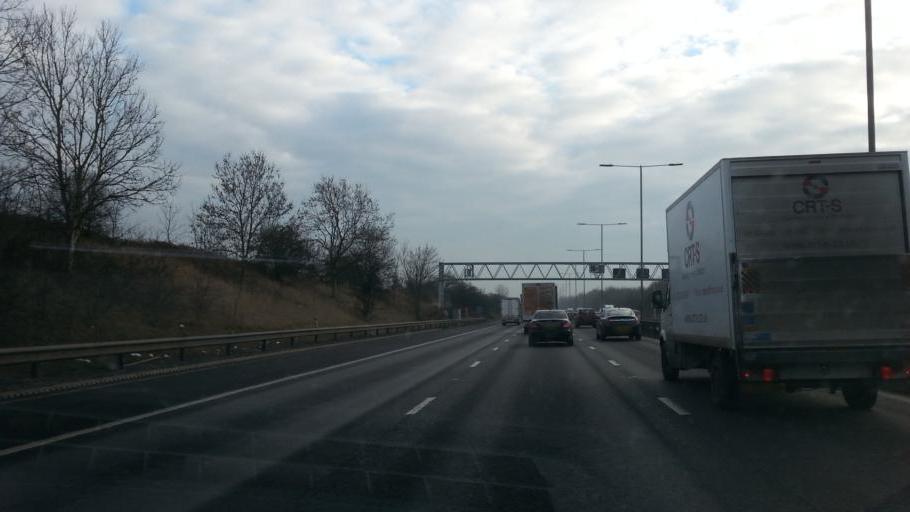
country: GB
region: England
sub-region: Warwickshire
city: Water Orton
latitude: 52.4982
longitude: -1.7373
